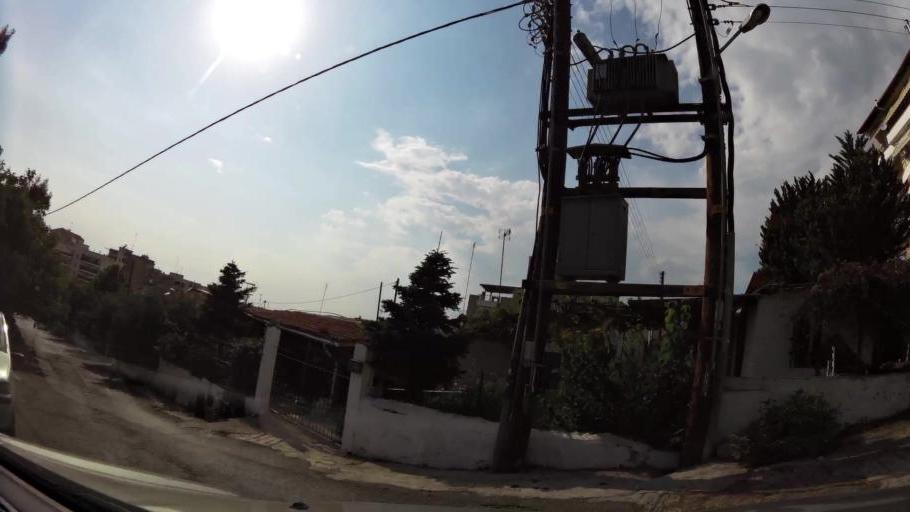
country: GR
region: Central Macedonia
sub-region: Nomos Thessalonikis
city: Polichni
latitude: 40.6601
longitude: 22.9595
